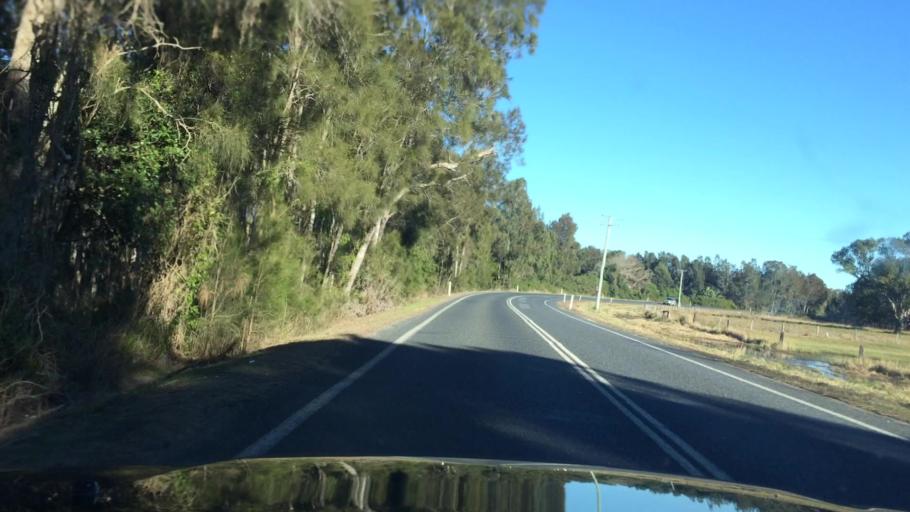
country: AU
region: New South Wales
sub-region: Port Macquarie-Hastings
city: North Shore
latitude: -31.4173
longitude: 152.8555
